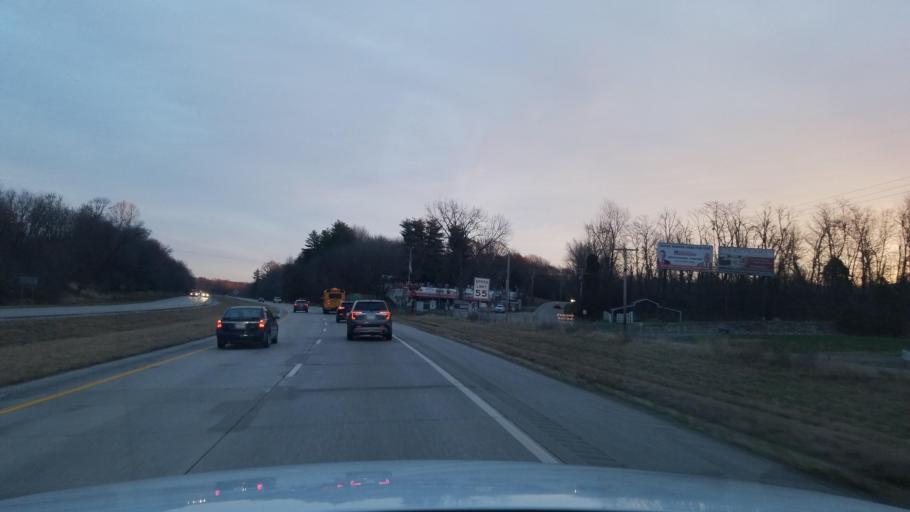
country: US
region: Indiana
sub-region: Vanderburgh County
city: Evansville
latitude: 37.9426
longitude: -87.7169
